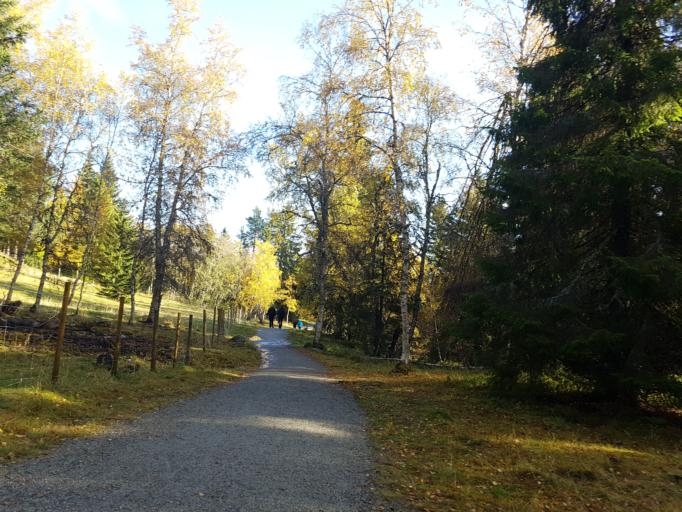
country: NO
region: Sor-Trondelag
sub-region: Trondheim
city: Trondheim
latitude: 63.4203
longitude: 10.3140
